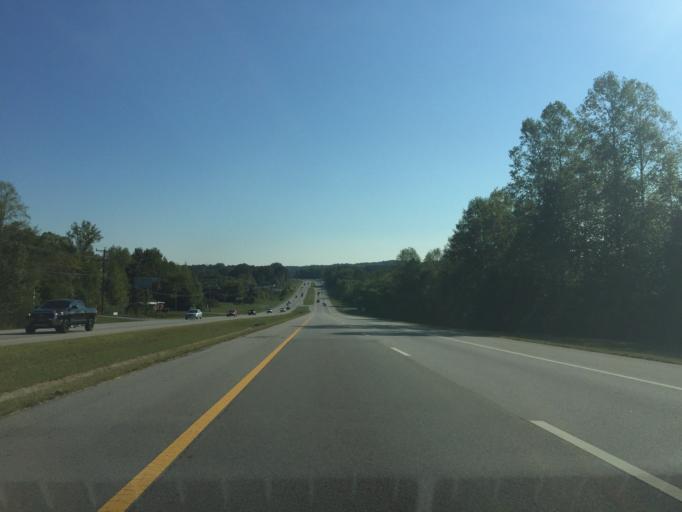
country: US
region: Tennessee
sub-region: Hamilton County
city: Harrison
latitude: 35.1053
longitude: -85.1568
